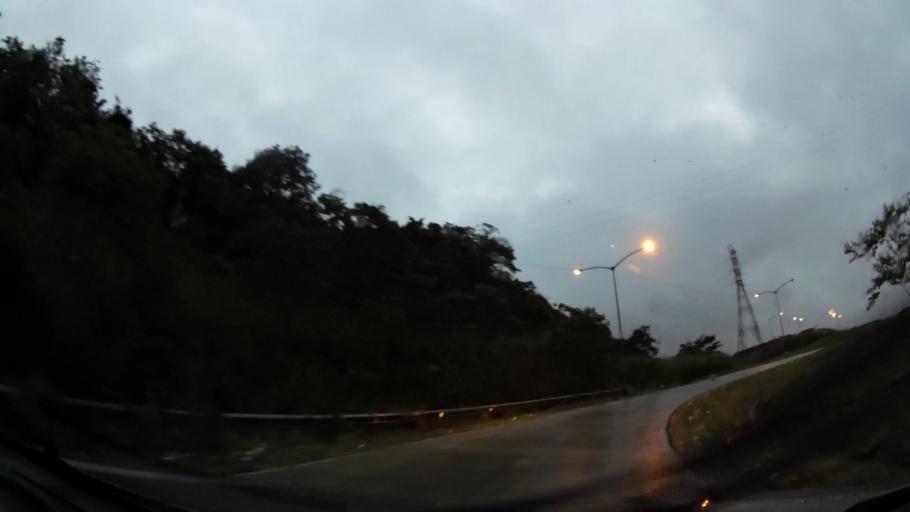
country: PA
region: Panama
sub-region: Distrito de Panama
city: Paraiso
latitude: 9.0374
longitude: -79.6306
